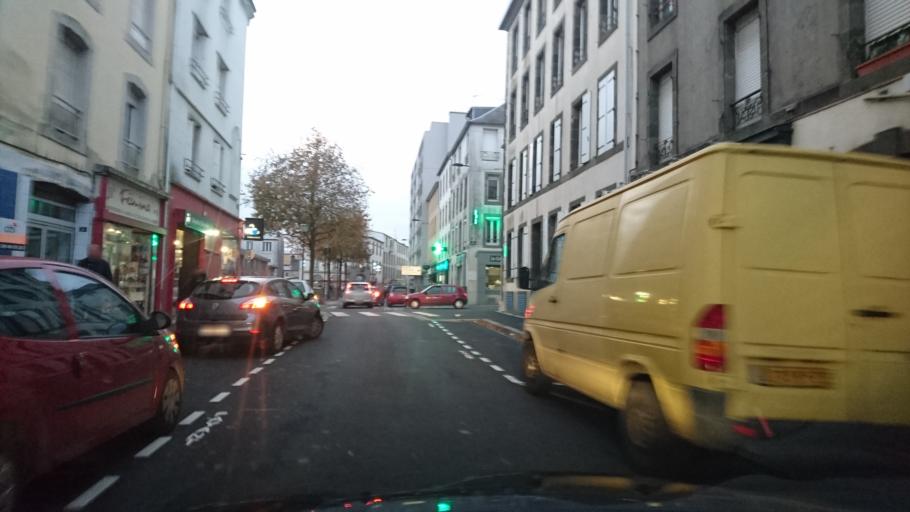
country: FR
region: Brittany
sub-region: Departement du Finistere
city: Brest
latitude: 48.3958
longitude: -4.4805
